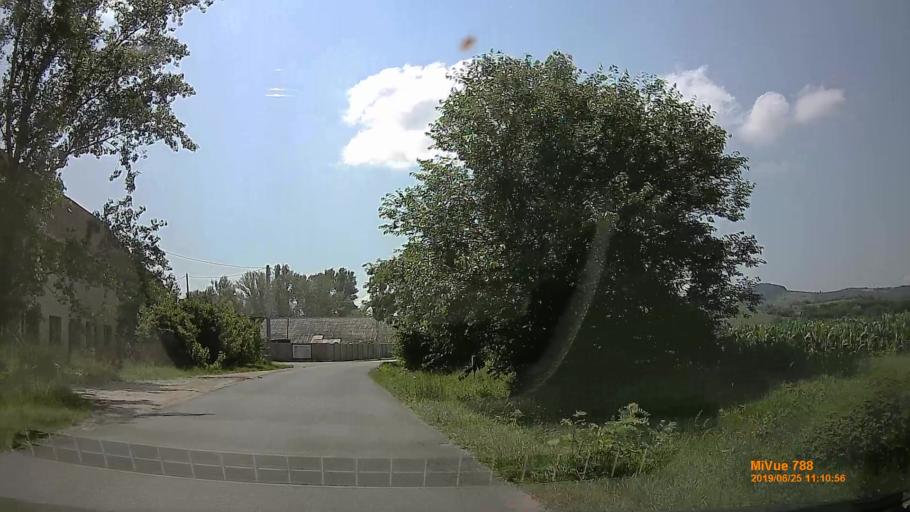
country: HU
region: Komarom-Esztergom
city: Tat
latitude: 47.7364
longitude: 18.6534
